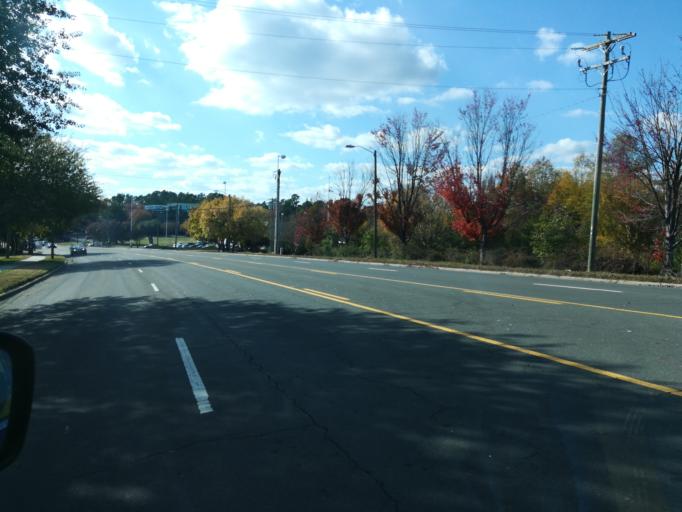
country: US
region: North Carolina
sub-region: Durham County
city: Durham
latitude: 35.9652
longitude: -78.9578
